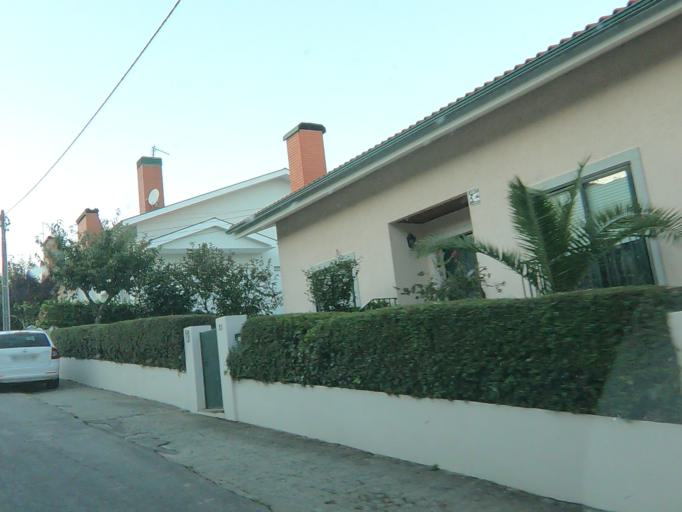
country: PT
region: Vila Real
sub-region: Vila Real
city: Vila Real
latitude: 41.3054
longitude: -7.7641
